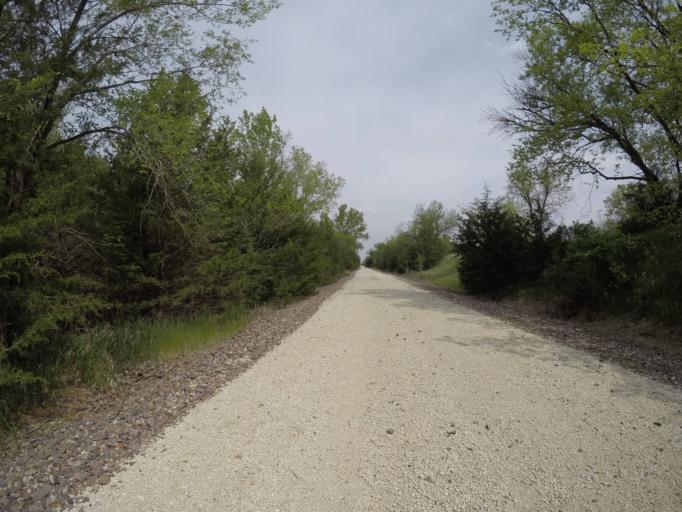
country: US
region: Nebraska
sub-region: Gage County
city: Wymore
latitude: 40.2020
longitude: -96.6605
